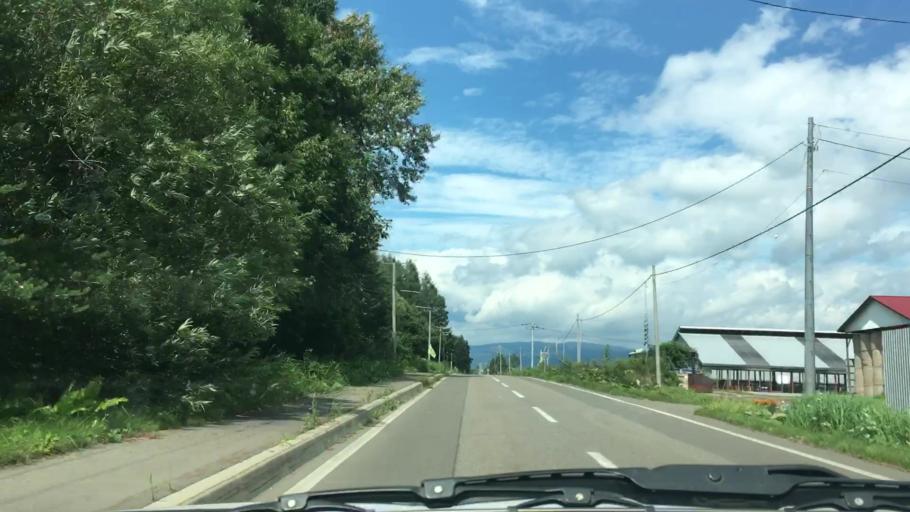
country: JP
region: Hokkaido
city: Otofuke
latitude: 43.2680
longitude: 143.3862
